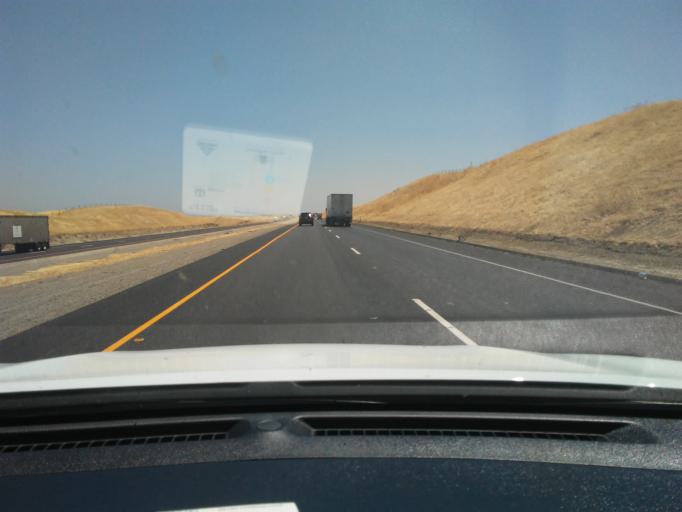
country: US
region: California
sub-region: San Joaquin County
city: Tracy
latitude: 37.6975
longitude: -121.4992
